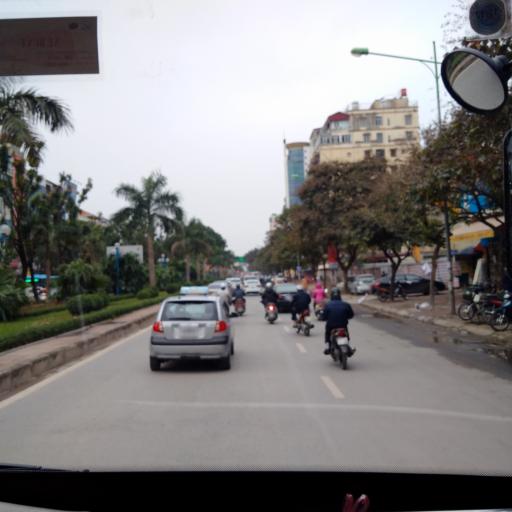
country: VN
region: Ha Noi
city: Cau Giay
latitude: 21.0461
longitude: 105.7956
